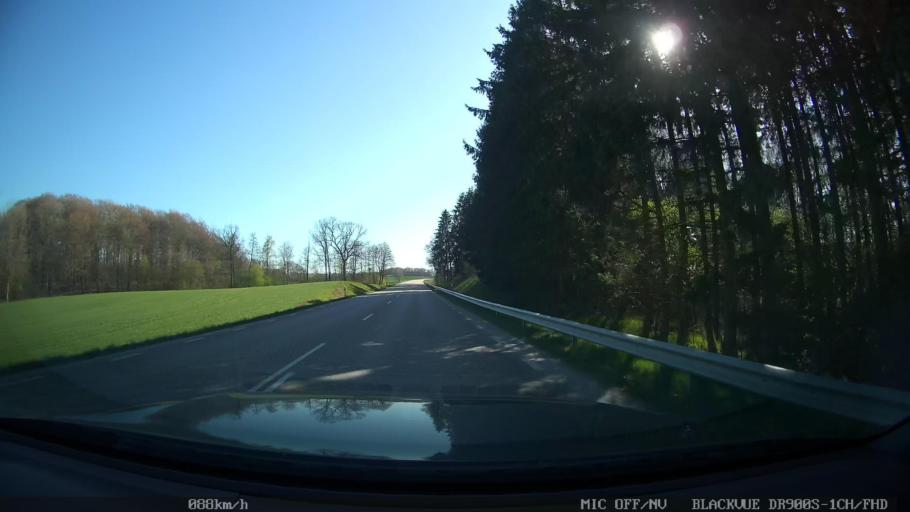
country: SE
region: Skane
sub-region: Klippans Kommun
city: Ljungbyhed
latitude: 55.9818
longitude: 13.2713
